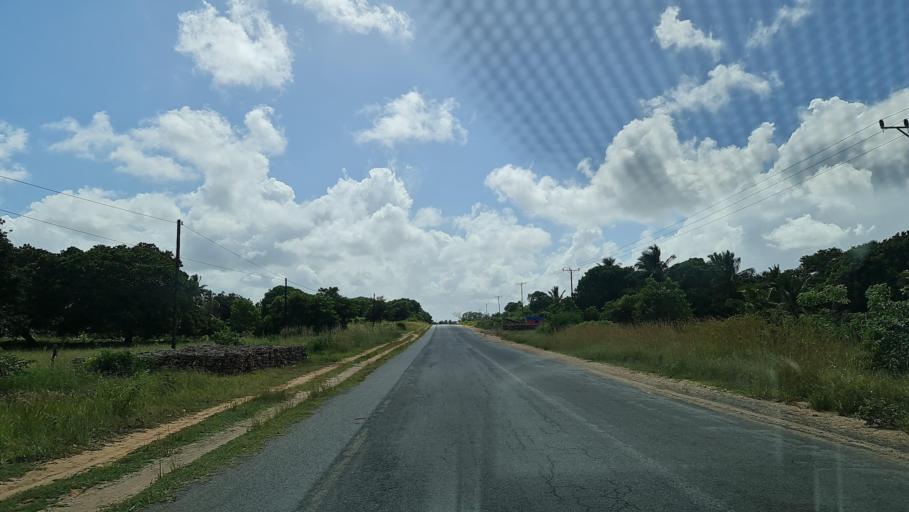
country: MZ
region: Gaza
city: Manjacaze
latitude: -24.6757
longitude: 34.5671
